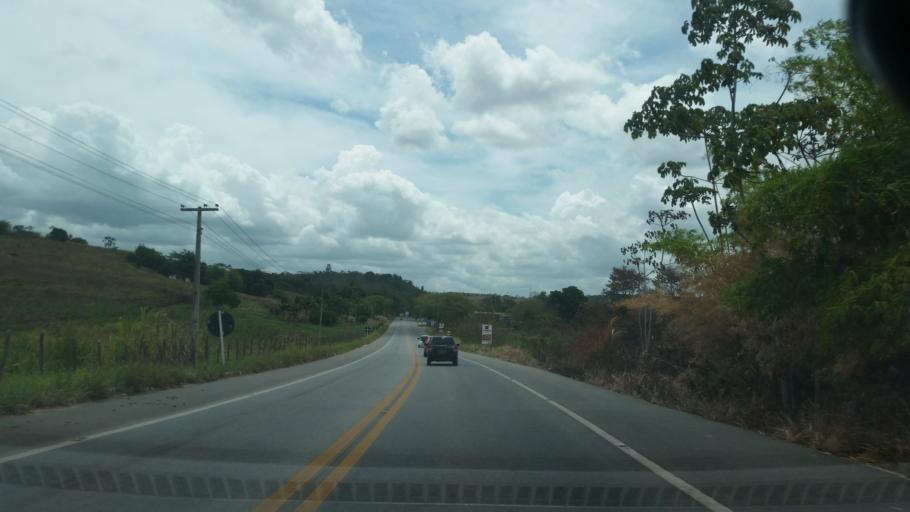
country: BR
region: Alagoas
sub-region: Uniao Dos Palmares
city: Uniao dos Palmares
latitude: -9.1829
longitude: -36.0359
